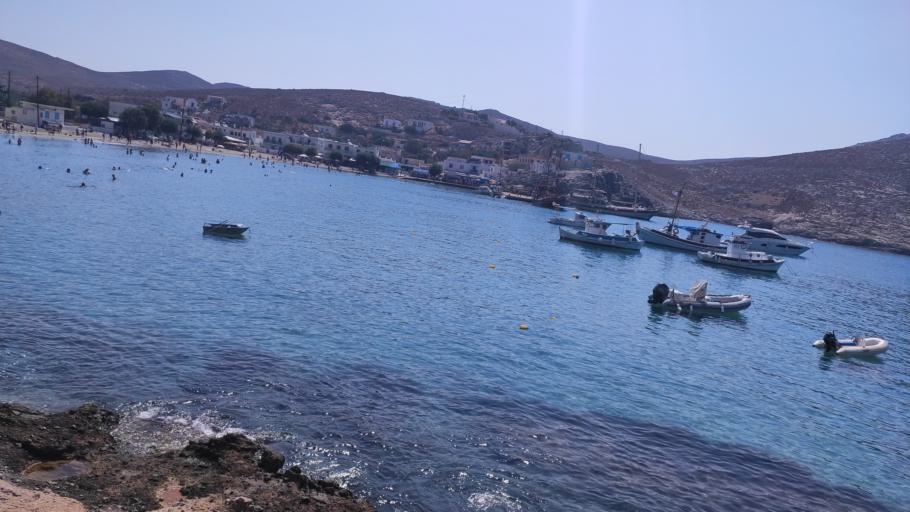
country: GR
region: South Aegean
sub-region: Nomos Dodekanisou
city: Pylion
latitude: 36.9328
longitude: 27.1316
